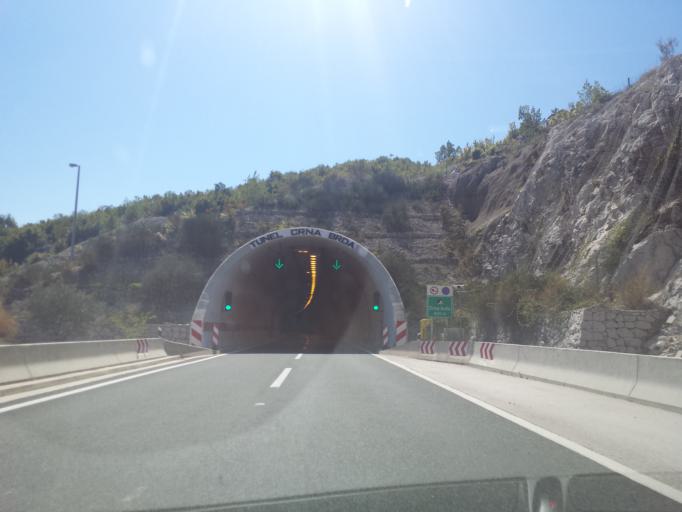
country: HR
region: Splitsko-Dalmatinska
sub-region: Grad Omis
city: Omis
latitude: 43.4865
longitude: 16.8005
